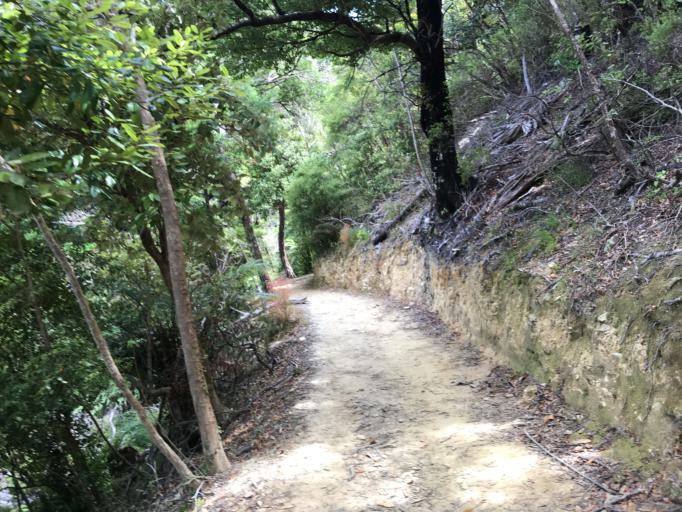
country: NZ
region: Marlborough
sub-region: Marlborough District
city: Picton
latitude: -41.1214
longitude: 174.1921
